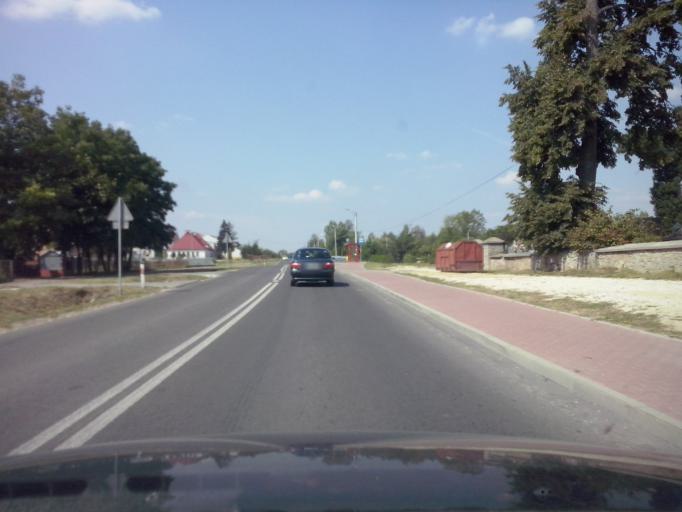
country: PL
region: Swietokrzyskie
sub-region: Powiat buski
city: Gnojno
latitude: 50.6031
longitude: 20.8448
